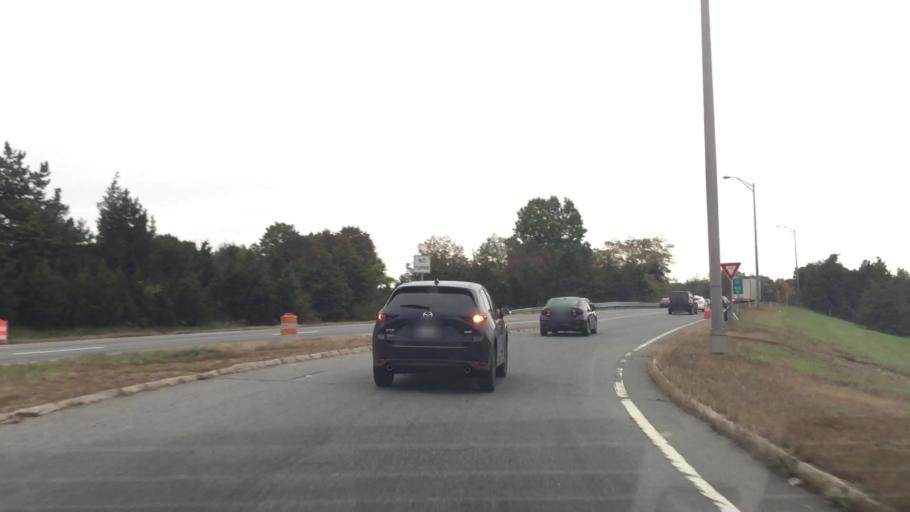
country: US
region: Massachusetts
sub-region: Essex County
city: Lawrence
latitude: 42.6625
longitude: -71.1957
